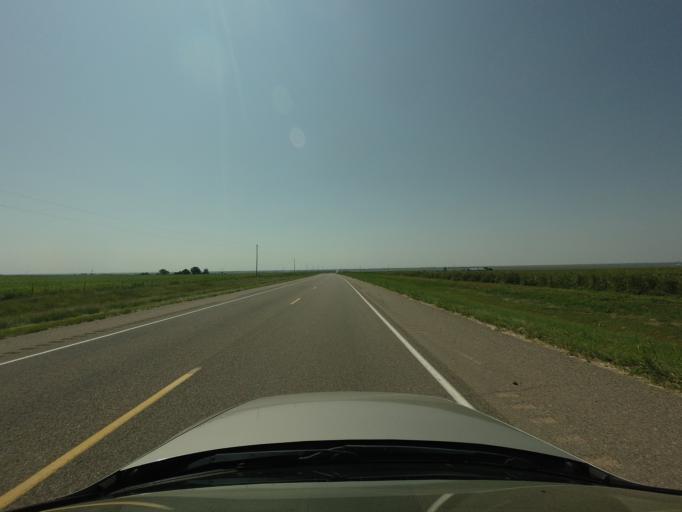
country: US
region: New Mexico
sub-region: Curry County
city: Clovis
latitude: 34.5544
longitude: -103.1967
